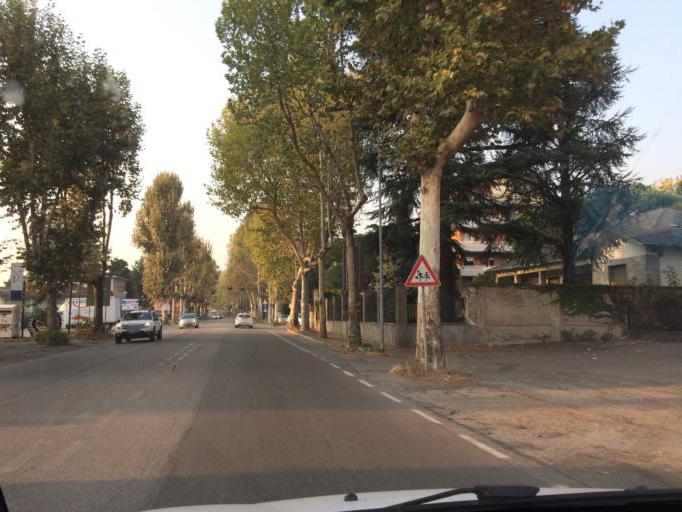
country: IT
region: Lombardy
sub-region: Provincia di Varese
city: Castellanza
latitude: 45.6094
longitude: 8.8892
